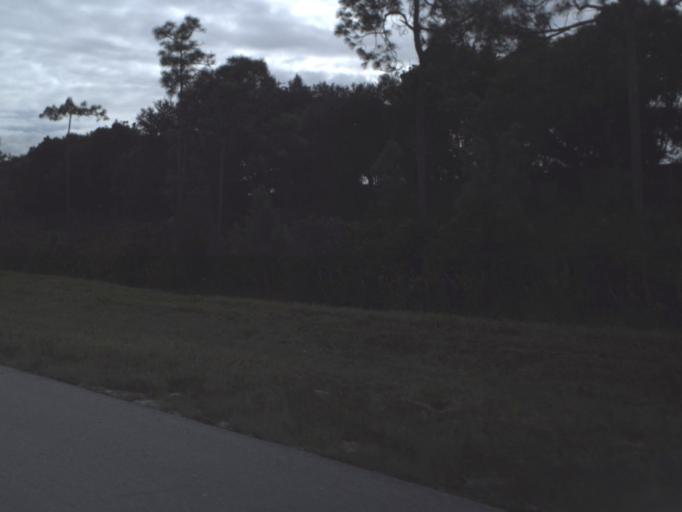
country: US
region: Florida
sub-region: Lee County
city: Estero
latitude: 26.4149
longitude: -81.7736
